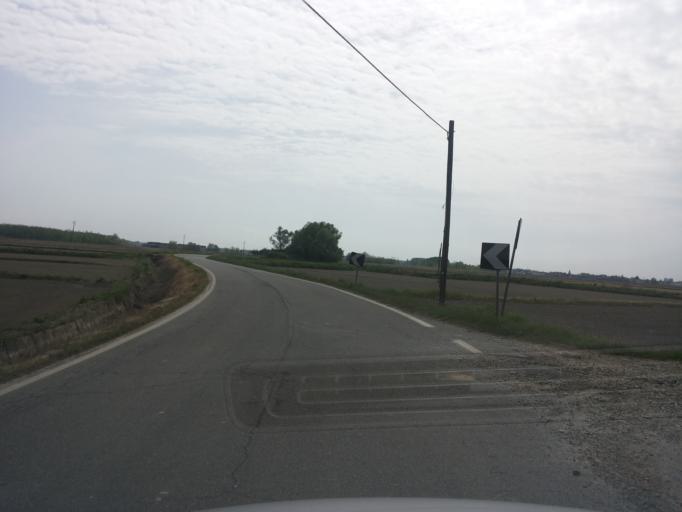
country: IT
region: Piedmont
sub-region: Provincia di Vercelli
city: Caresana
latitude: 45.2096
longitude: 8.5089
